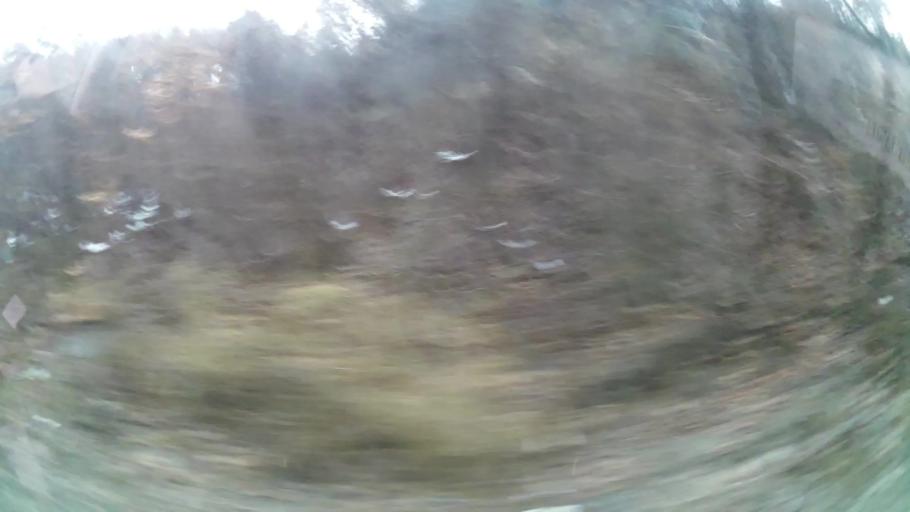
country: XK
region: Ferizaj
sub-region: Hani i Elezit
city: Hani i Elezit
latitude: 42.1715
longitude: 21.2758
